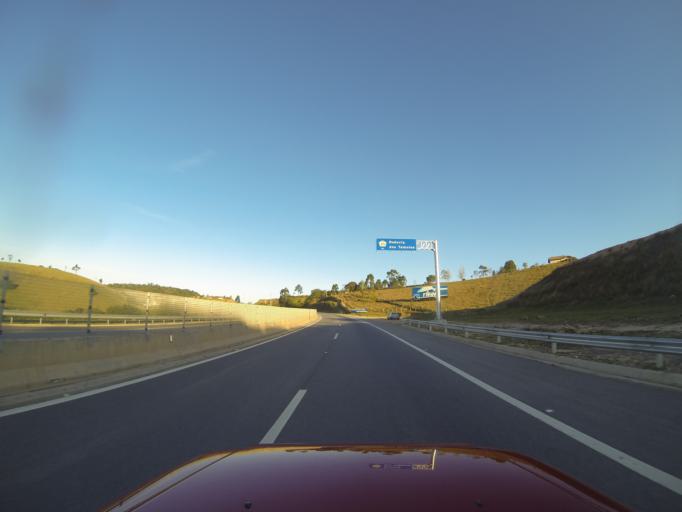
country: BR
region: Sao Paulo
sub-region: Santa Branca
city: Santa Branca
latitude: -23.4230
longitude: -45.6365
